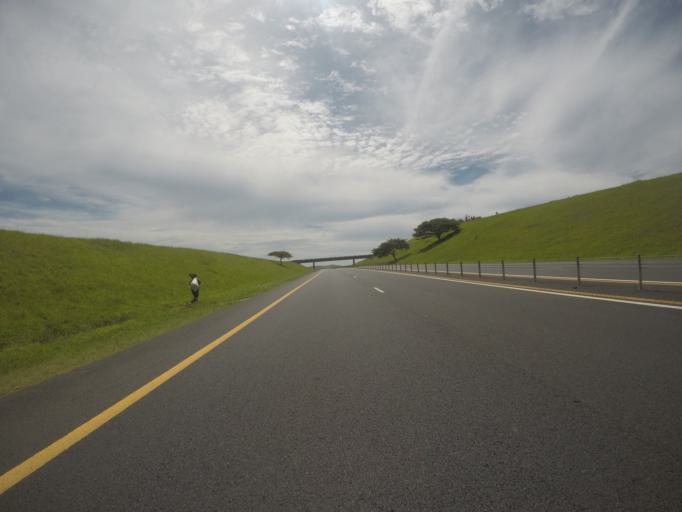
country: ZA
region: KwaZulu-Natal
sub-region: iLembe District Municipality
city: Mandeni
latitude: -29.1773
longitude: 31.5054
